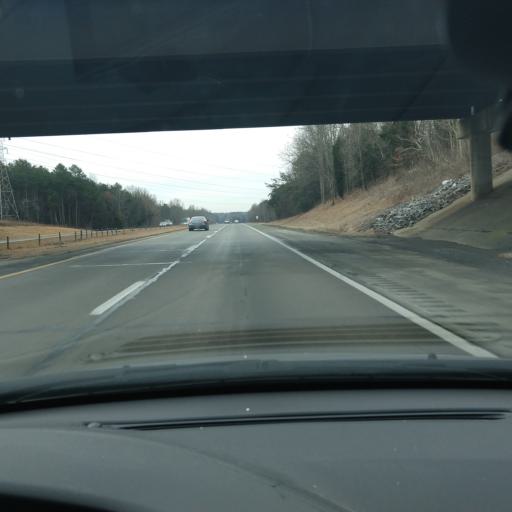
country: US
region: North Carolina
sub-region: Davidson County
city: Midway
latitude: 36.0068
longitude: -80.2366
